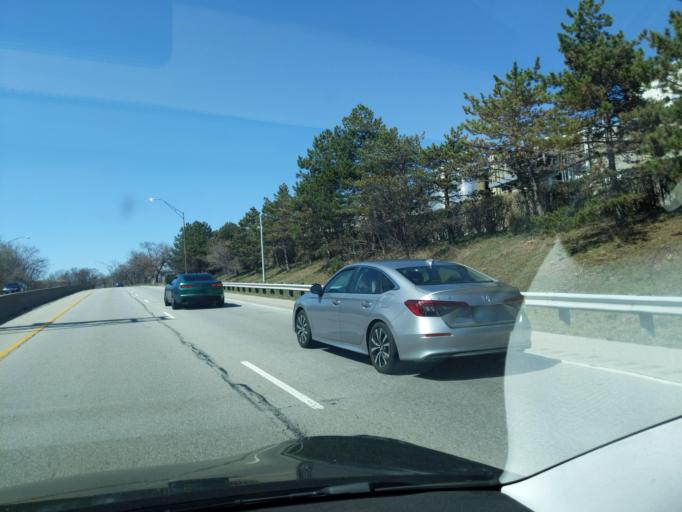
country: US
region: Ohio
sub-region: Hamilton County
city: Cincinnati
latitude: 39.1645
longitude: -84.4375
